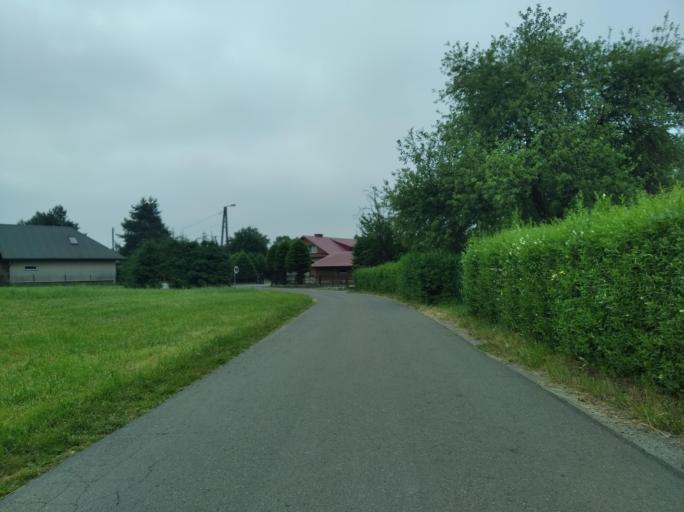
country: PL
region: Subcarpathian Voivodeship
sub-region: Powiat brzozowski
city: Jablonica Polska
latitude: 49.6843
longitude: 21.8888
